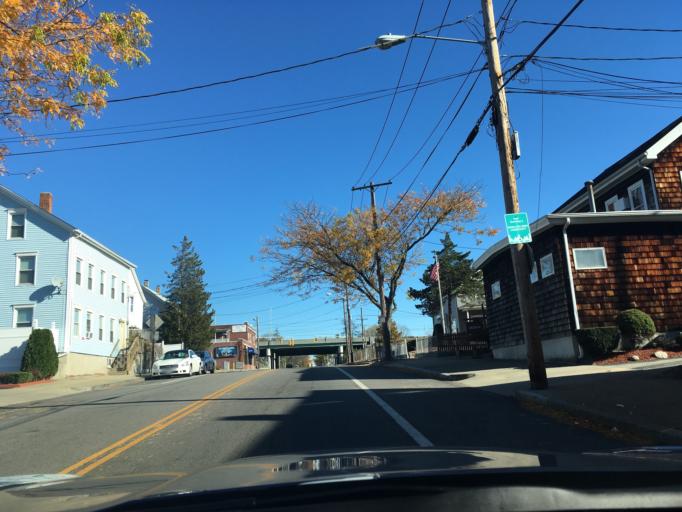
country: US
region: Rhode Island
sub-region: Providence County
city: Central Falls
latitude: 41.8901
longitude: -71.3811
